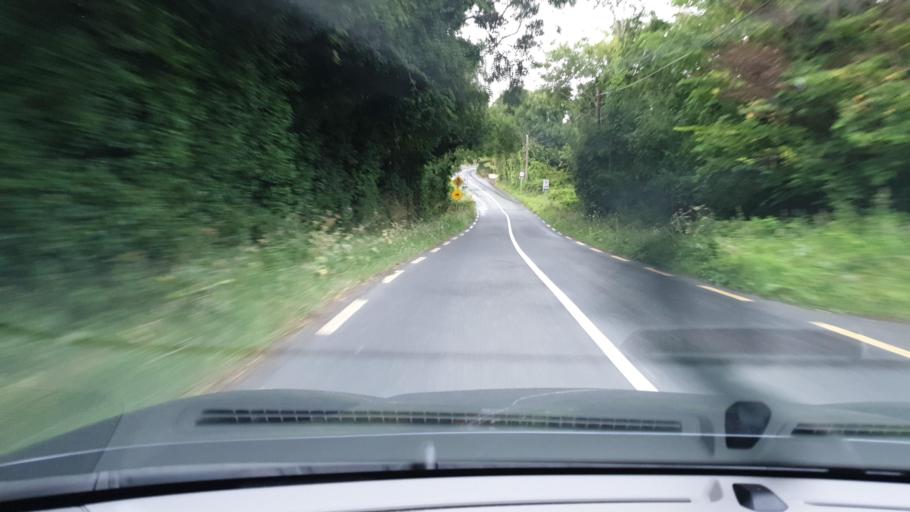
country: IE
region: Leinster
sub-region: South Dublin
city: Rathcoole
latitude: 53.2460
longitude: -6.5105
